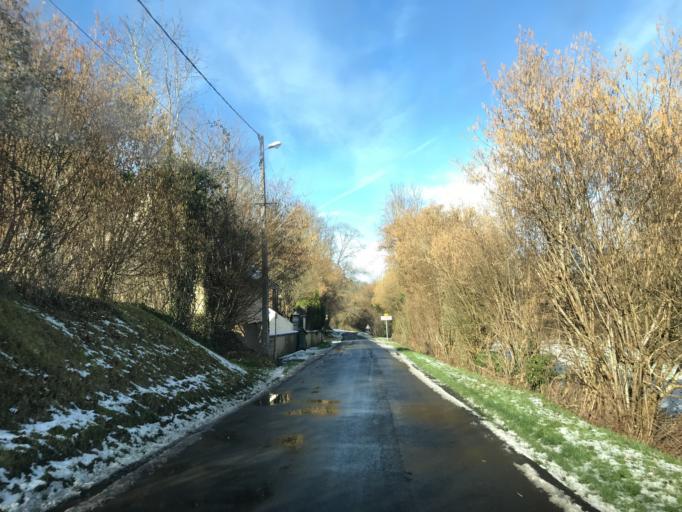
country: FR
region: Haute-Normandie
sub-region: Departement de l'Eure
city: Houlbec-Cocherel
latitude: 49.0754
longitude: 1.2820
